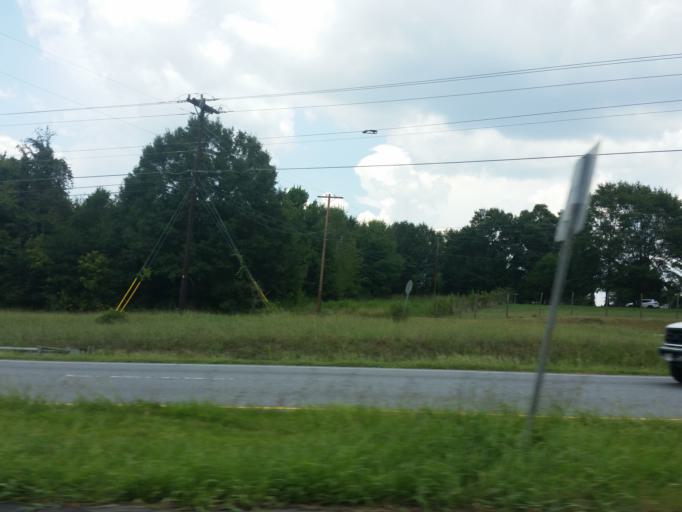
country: US
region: North Carolina
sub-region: Cleveland County
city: White Plains
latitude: 35.2513
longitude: -81.4519
